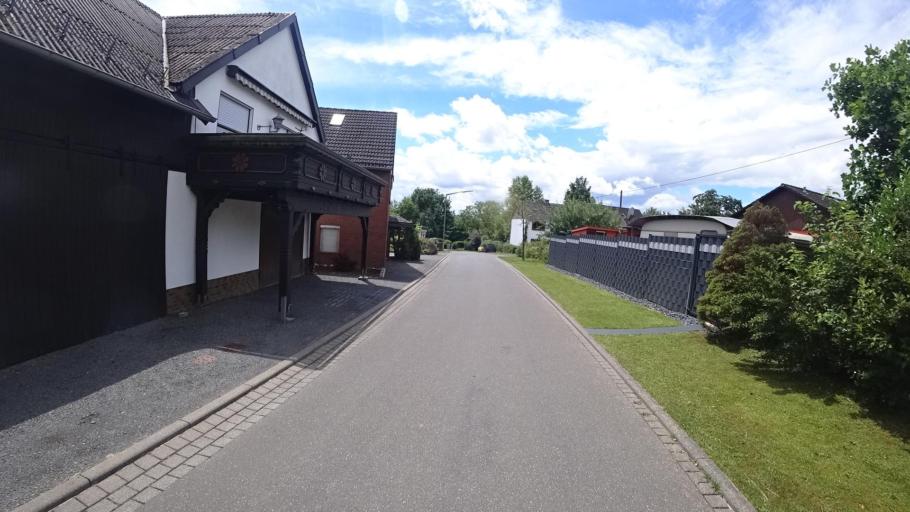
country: DE
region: Rheinland-Pfalz
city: Seifen
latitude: 50.6704
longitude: 7.5145
